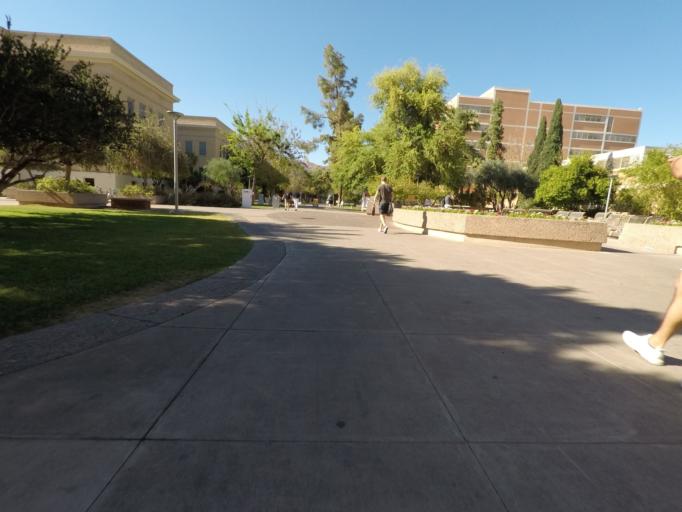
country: US
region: Arizona
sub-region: Maricopa County
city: Tempe Junction
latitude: 33.4201
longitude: -111.9350
